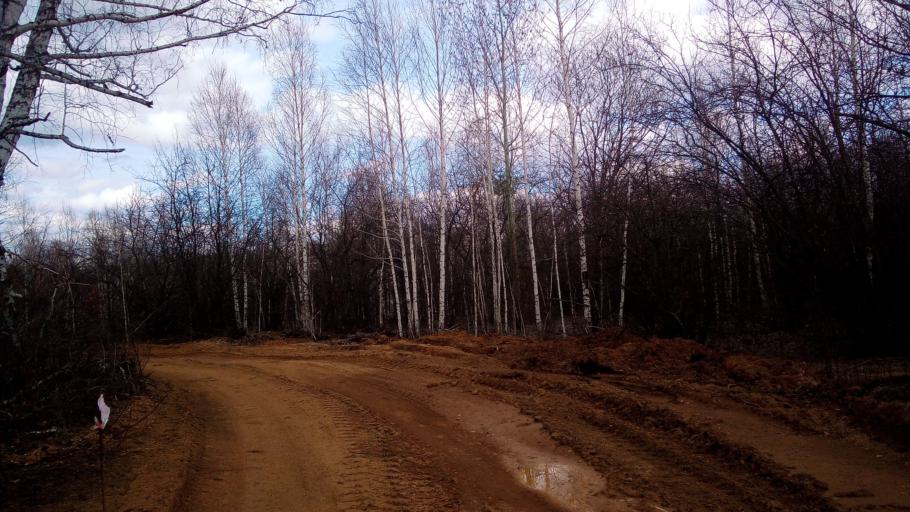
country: RU
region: Chelyabinsk
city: Sargazy
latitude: 55.1243
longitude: 61.2578
